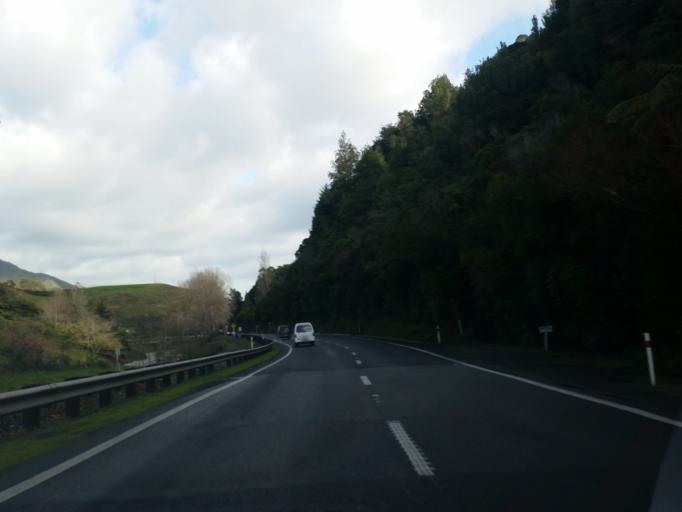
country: NZ
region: Waikato
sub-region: Hauraki District
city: Waihi
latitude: -37.4167
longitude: 175.7676
